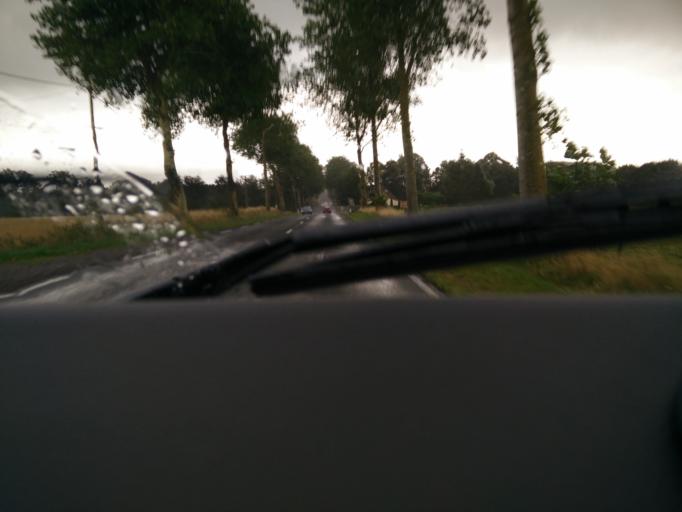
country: FR
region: Nord-Pas-de-Calais
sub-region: Departement du Pas-de-Calais
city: Savy-Berlette
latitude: 50.3488
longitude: 2.5431
